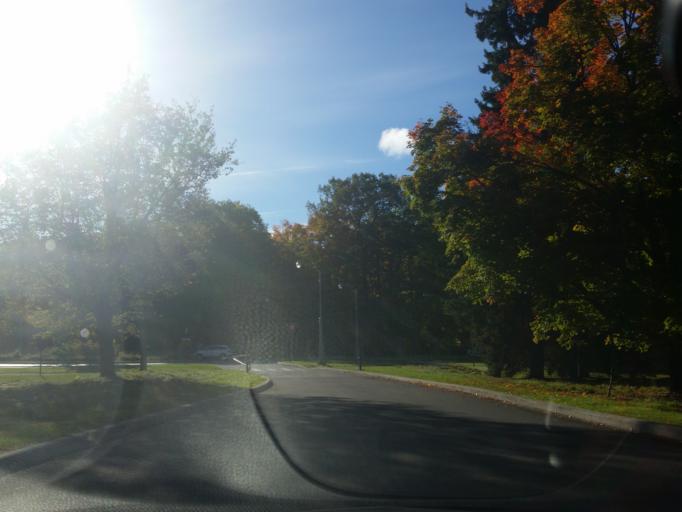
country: CA
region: Quebec
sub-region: Outaouais
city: Gatineau
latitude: 45.4464
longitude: -75.6899
